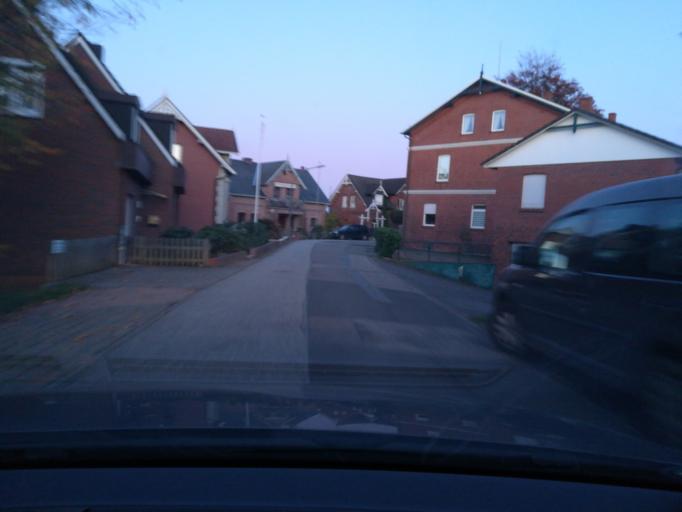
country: DE
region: Lower Saxony
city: Winsen
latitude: 53.4002
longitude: 10.1773
